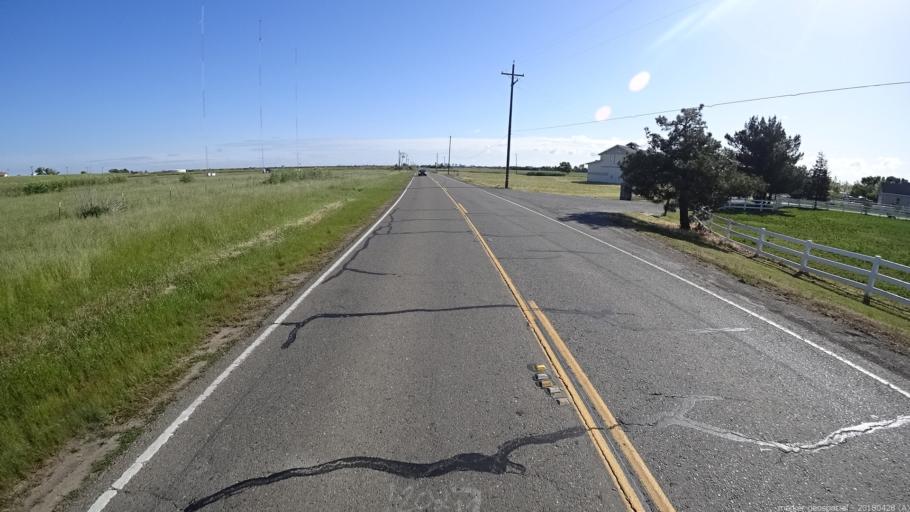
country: US
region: California
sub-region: Yolo County
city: West Sacramento
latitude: 38.5058
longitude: -121.5810
